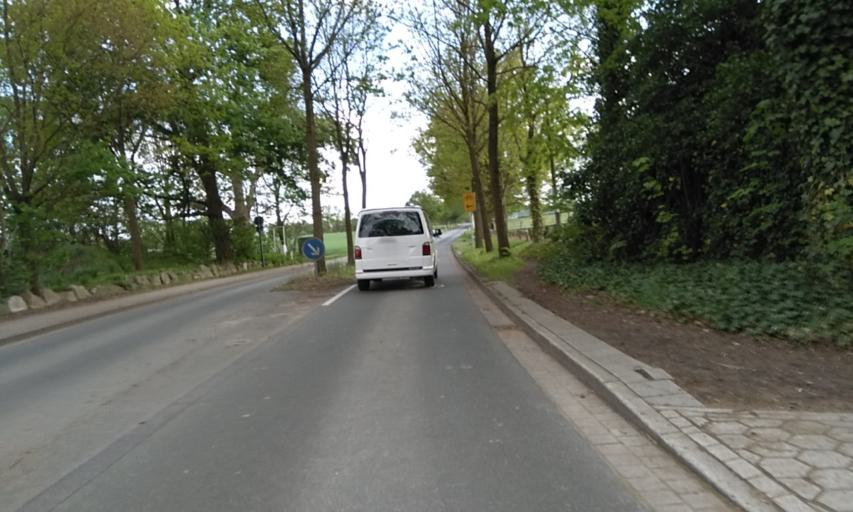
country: DE
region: Lower Saxony
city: Buxtehude
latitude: 53.4466
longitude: 9.6668
